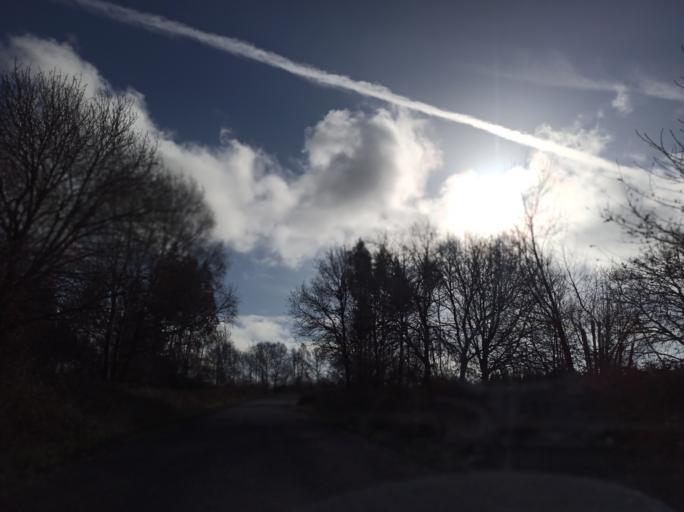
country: ES
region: Galicia
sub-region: Provincia da Coruna
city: Sobrado
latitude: 43.0850
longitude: -7.9644
